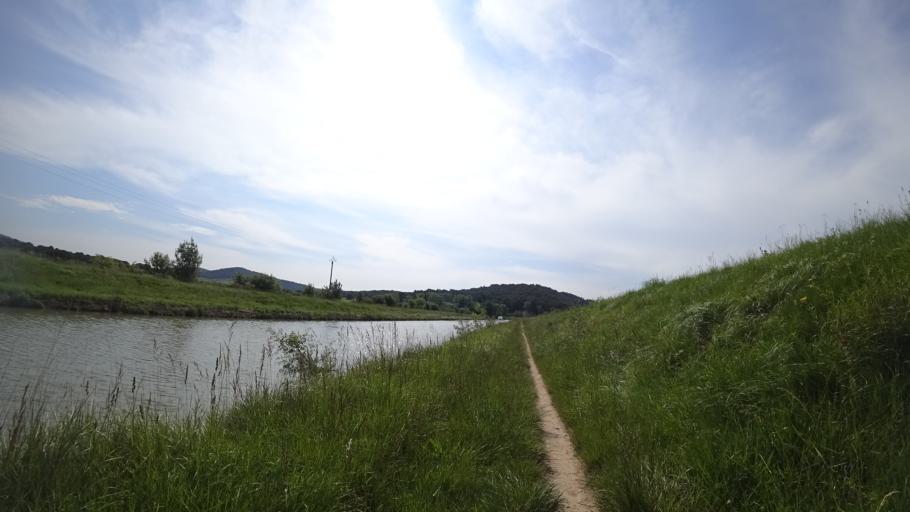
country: FR
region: Languedoc-Roussillon
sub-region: Departement de l'Herault
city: Olonzac
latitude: 43.2638
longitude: 2.7457
